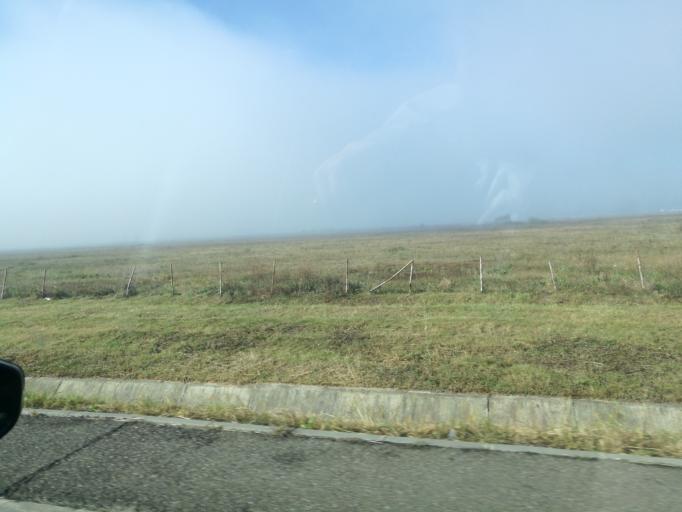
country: RO
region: Iasi
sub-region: Comuna Valea Lupului
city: Valea Lupului
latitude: 47.1687
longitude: 27.5098
